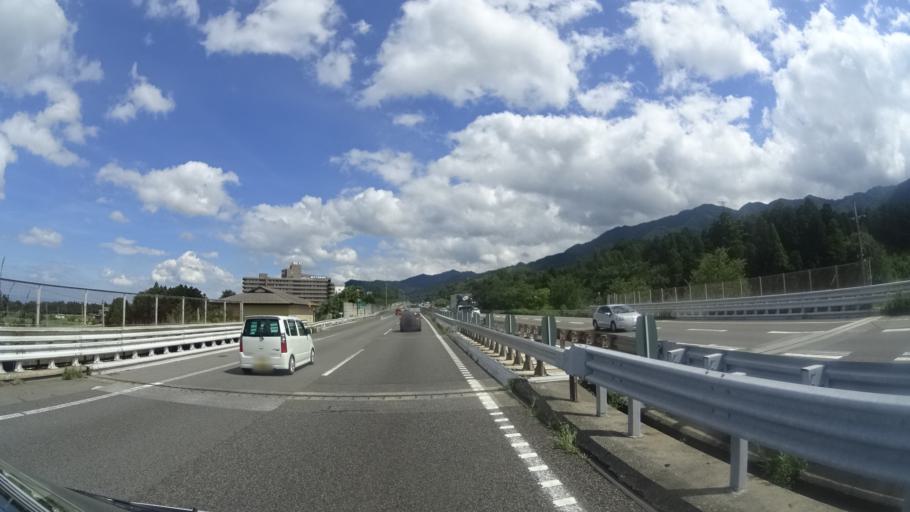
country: JP
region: Shiga Prefecture
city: Youkaichi
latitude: 35.1287
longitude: 136.2744
